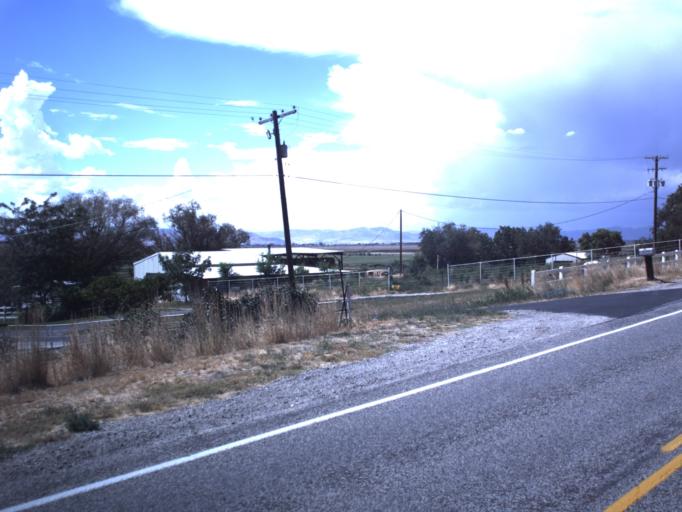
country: US
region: Utah
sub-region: Box Elder County
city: Brigham City
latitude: 41.5503
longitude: -112.0183
